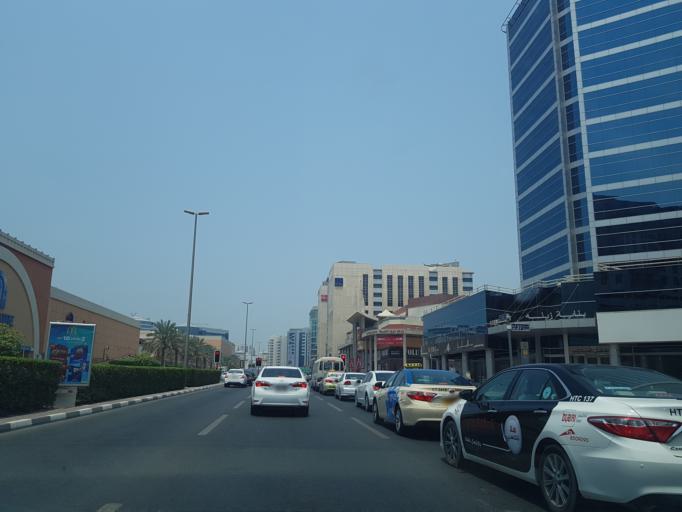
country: AE
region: Ash Shariqah
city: Sharjah
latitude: 25.2521
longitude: 55.3344
